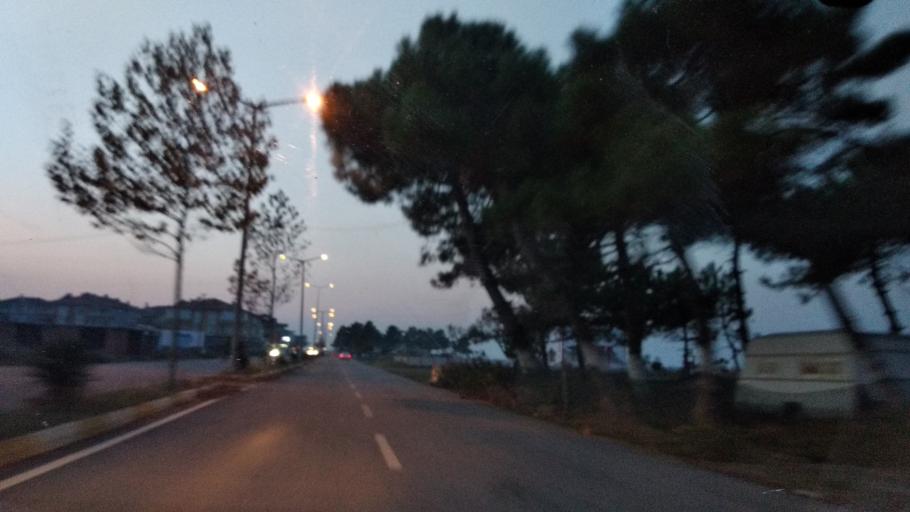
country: TR
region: Sakarya
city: Karasu
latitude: 41.0938
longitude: 30.7356
